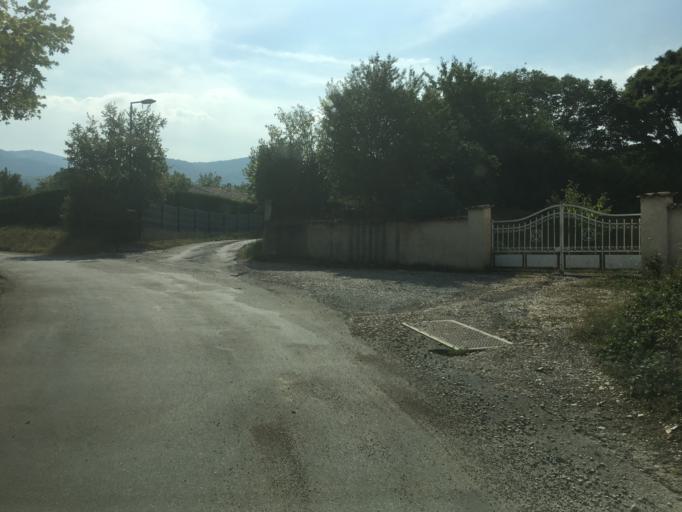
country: FR
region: Provence-Alpes-Cote d'Azur
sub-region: Departement des Alpes-de-Haute-Provence
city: Mallemoisson
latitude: 43.9392
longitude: 6.1721
